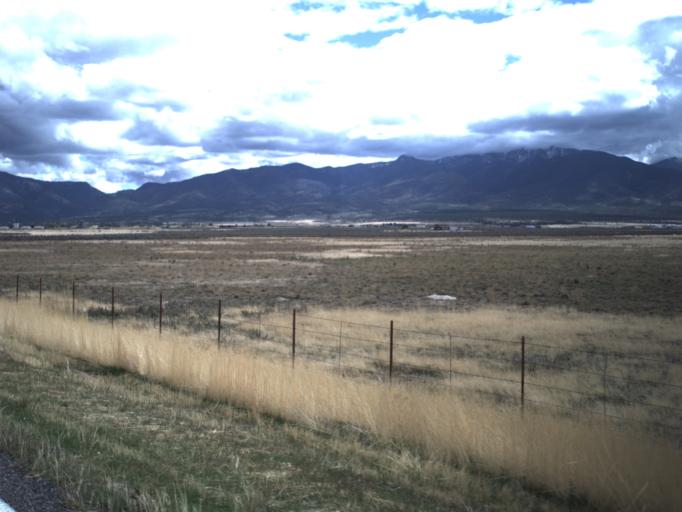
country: US
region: Utah
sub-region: Millard County
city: Fillmore
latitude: 38.9791
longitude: -112.3763
